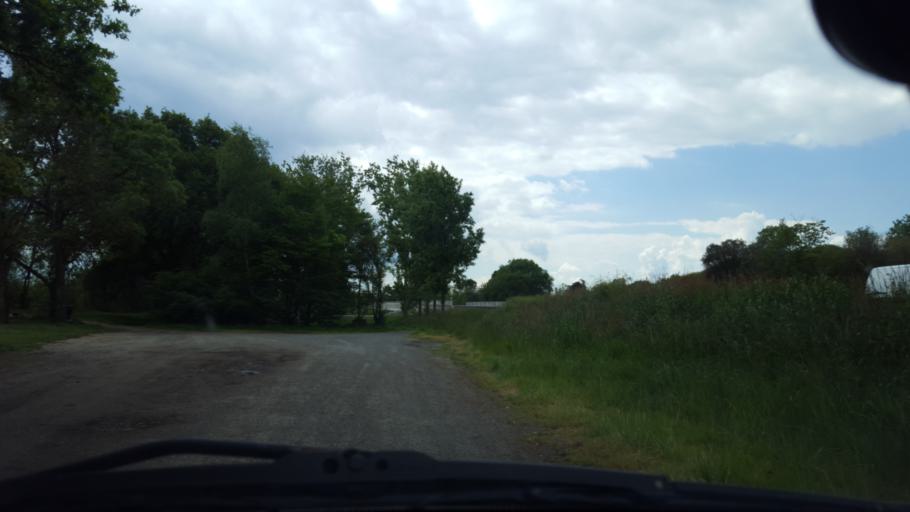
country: FR
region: Pays de la Loire
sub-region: Departement de la Loire-Atlantique
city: Saint-Philbert-de-Grand-Lieu
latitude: 47.0461
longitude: -1.6453
